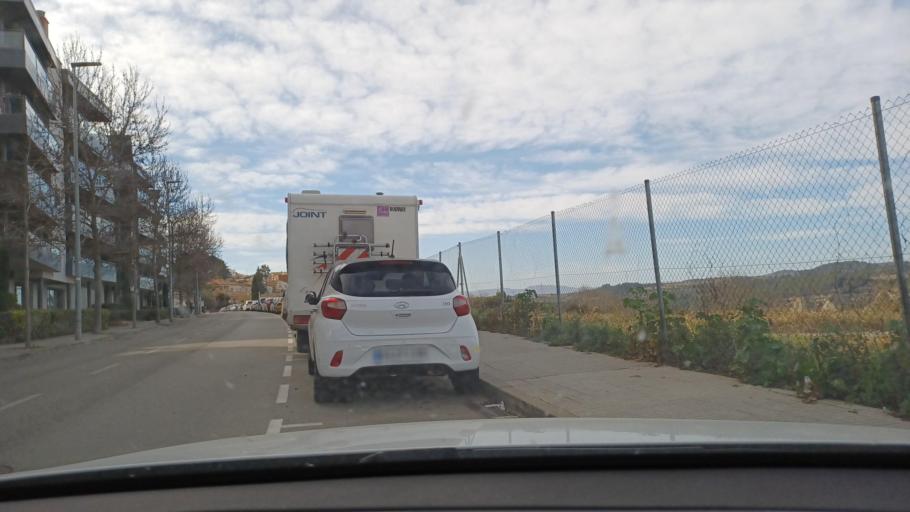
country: ES
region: Catalonia
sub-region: Provincia de Barcelona
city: Gelida
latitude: 41.4435
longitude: 1.8636
